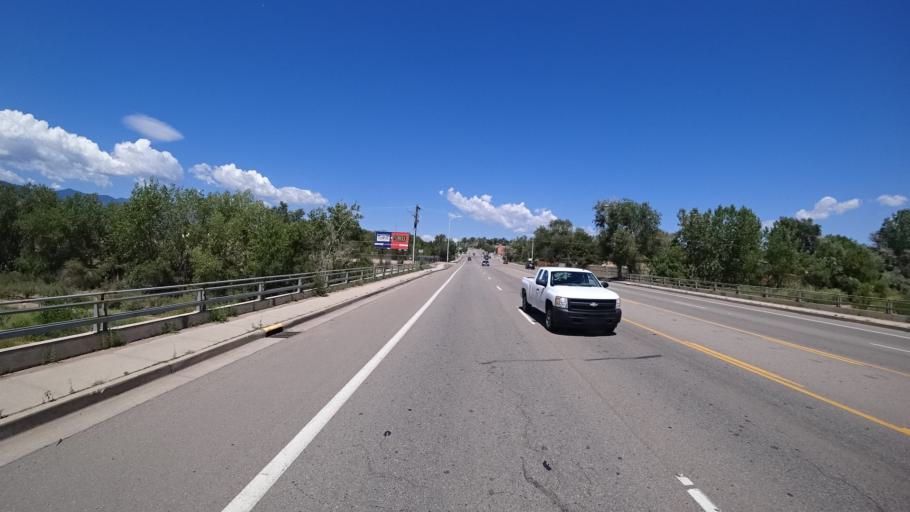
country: US
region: Colorado
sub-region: El Paso County
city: Stratmoor
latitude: 38.7924
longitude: -104.7654
